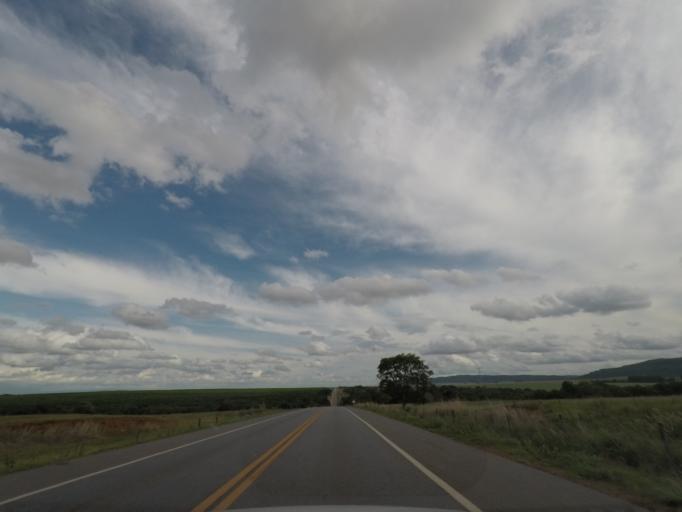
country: BR
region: Goias
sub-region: Barro Alto
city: Barro Alto
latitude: -15.2739
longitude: -48.6839
